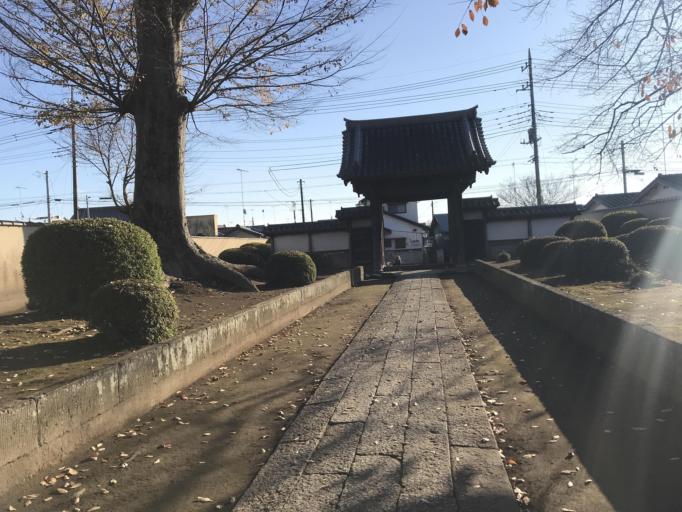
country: JP
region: Ibaraki
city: Yuki
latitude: 36.3050
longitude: 139.8715
